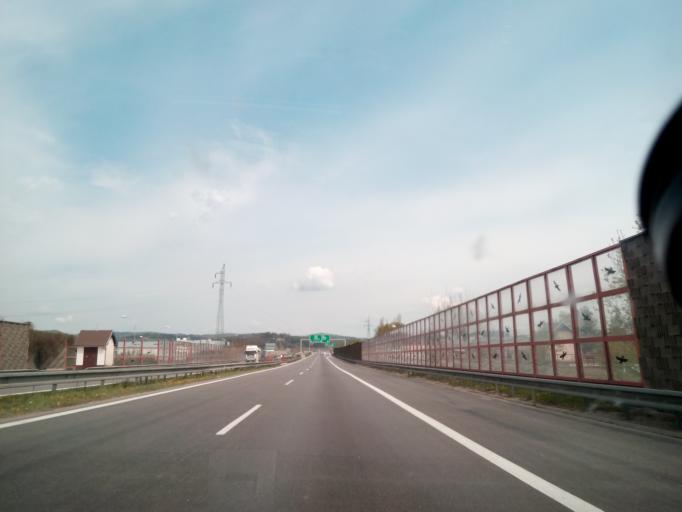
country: SK
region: Nitriansky
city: Puchov
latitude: 49.0562
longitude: 18.3290
